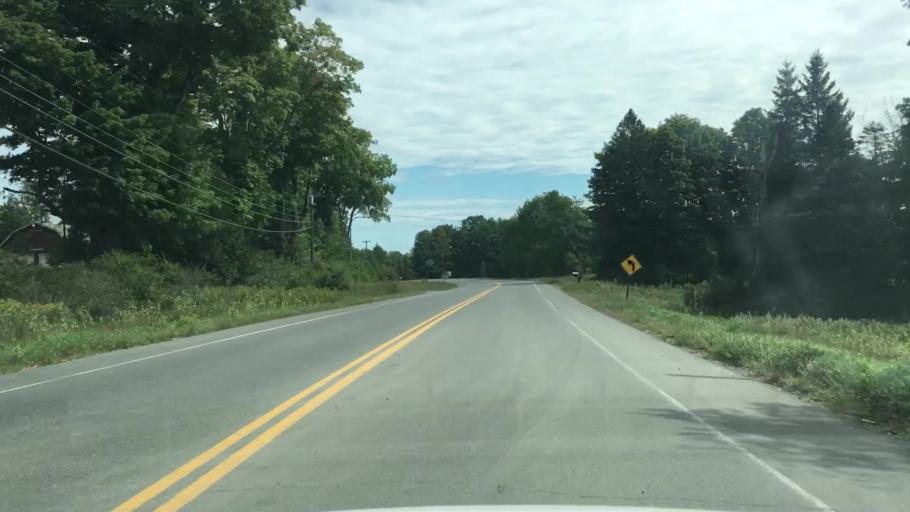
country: US
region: Maine
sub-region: Piscataquis County
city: Dover-Foxcroft
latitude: 45.2016
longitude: -69.1919
